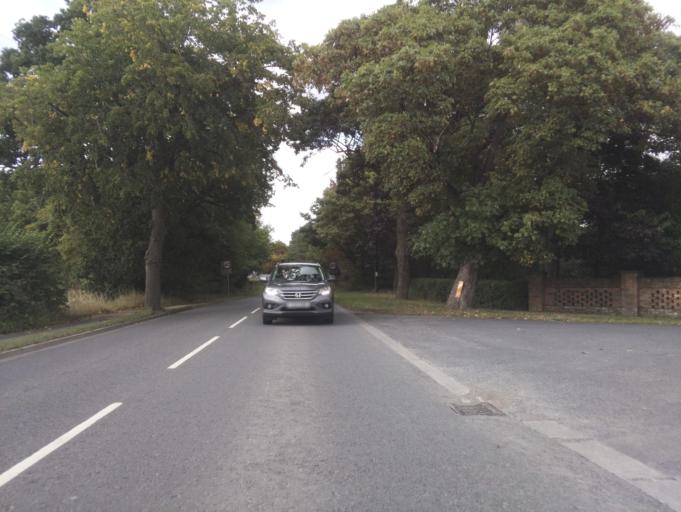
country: GB
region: England
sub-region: North Yorkshire
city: Ripon
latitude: 54.1502
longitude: -1.5314
